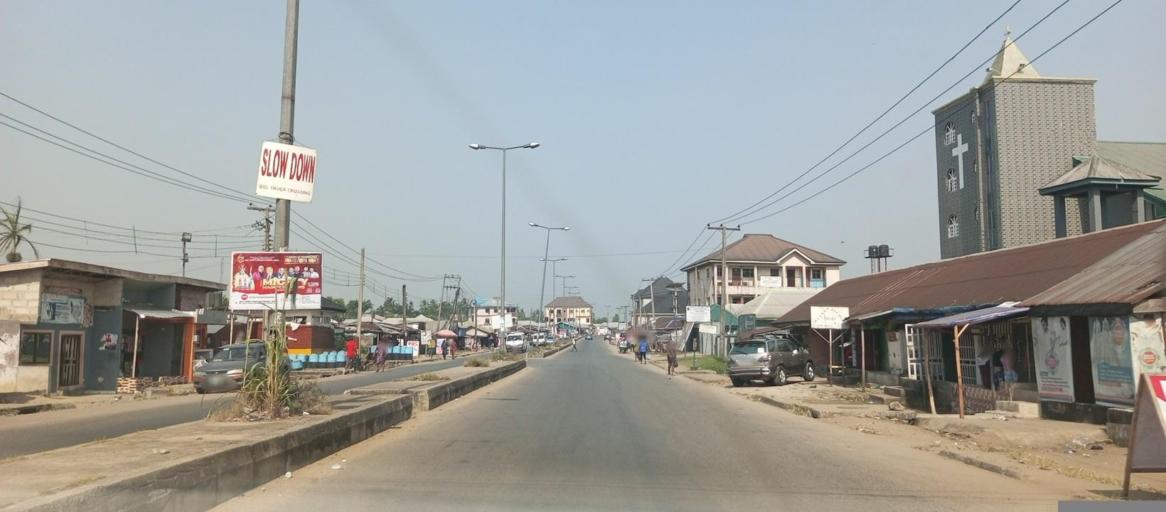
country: NG
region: Rivers
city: Emuoha
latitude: 4.8844
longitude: 6.9037
